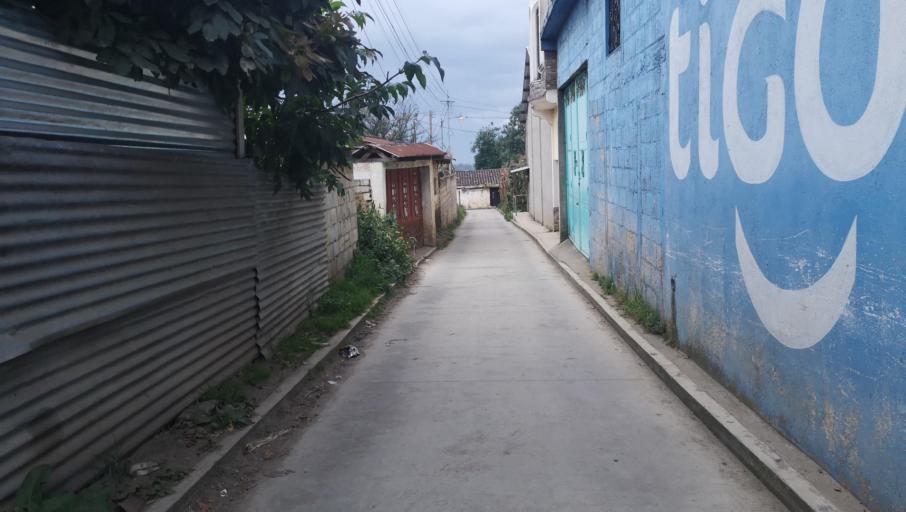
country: GT
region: Quetzaltenango
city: Cantel
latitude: 14.8187
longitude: -91.4345
